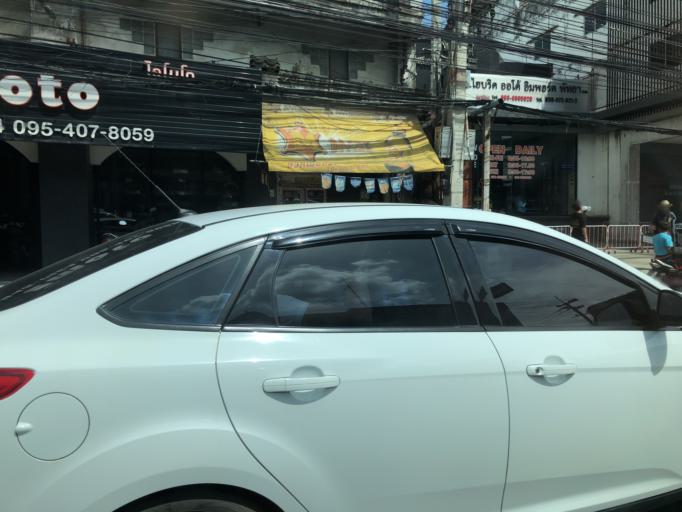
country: TH
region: Chon Buri
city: Phatthaya
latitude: 12.9671
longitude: 100.9101
